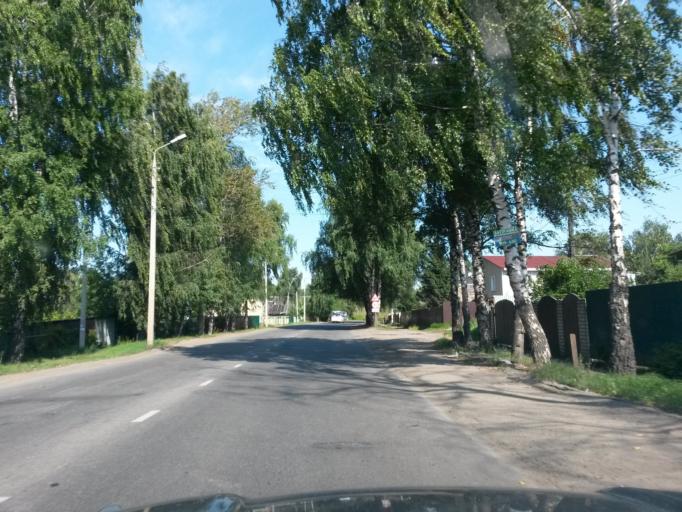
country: RU
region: Jaroslavl
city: Yaroslavl
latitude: 57.6495
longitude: 39.9073
